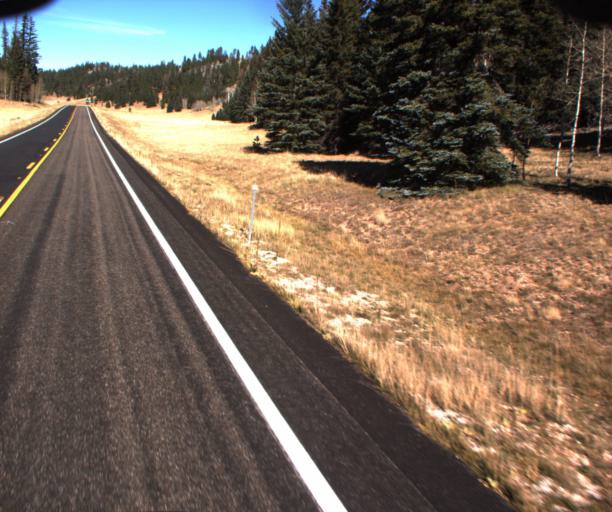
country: US
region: Arizona
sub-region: Coconino County
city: Grand Canyon
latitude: 36.4685
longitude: -112.1261
